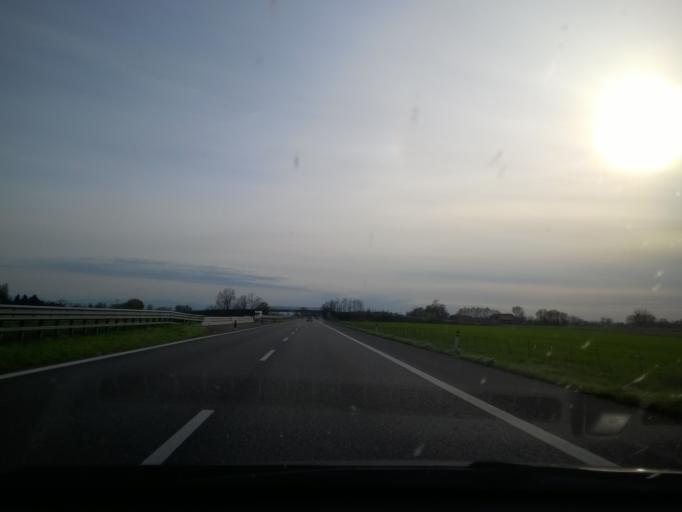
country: IT
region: Emilia-Romagna
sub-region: Provincia di Piacenza
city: Monticelli d'Ongina
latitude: 45.0719
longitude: 9.9640
